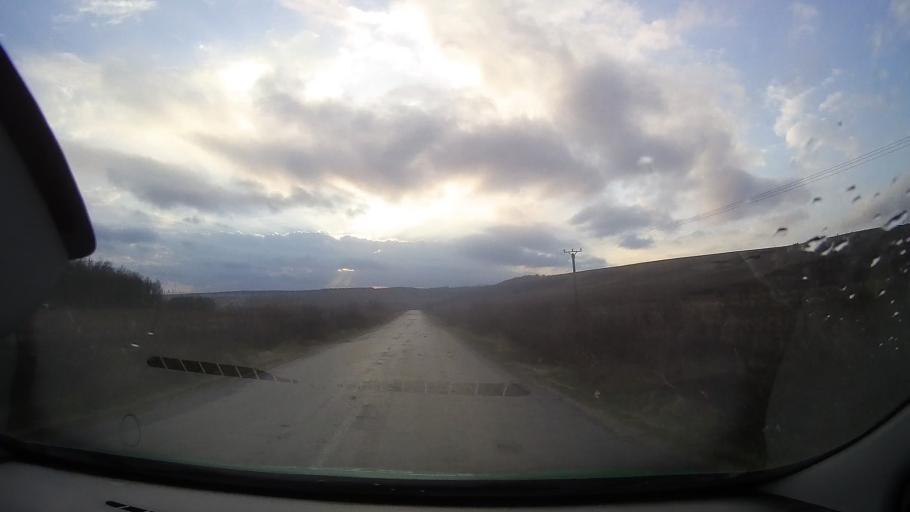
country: RO
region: Constanta
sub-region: Comuna Dobromir
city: Dobromir
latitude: 44.0341
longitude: 27.8403
